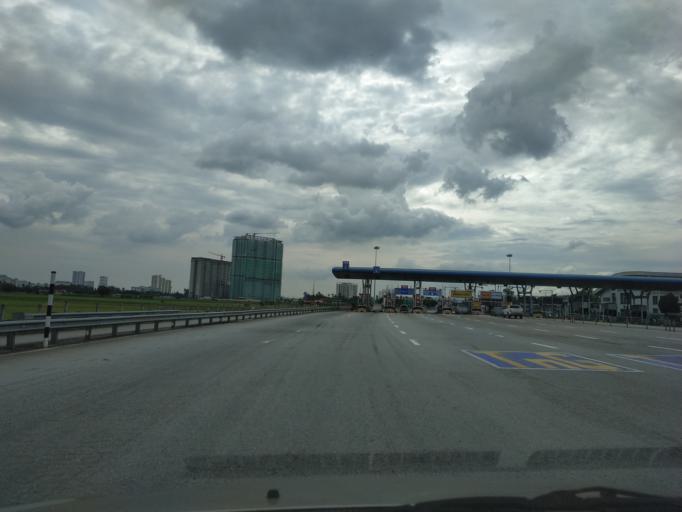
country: MY
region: Penang
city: Perai
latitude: 5.3986
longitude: 100.4259
